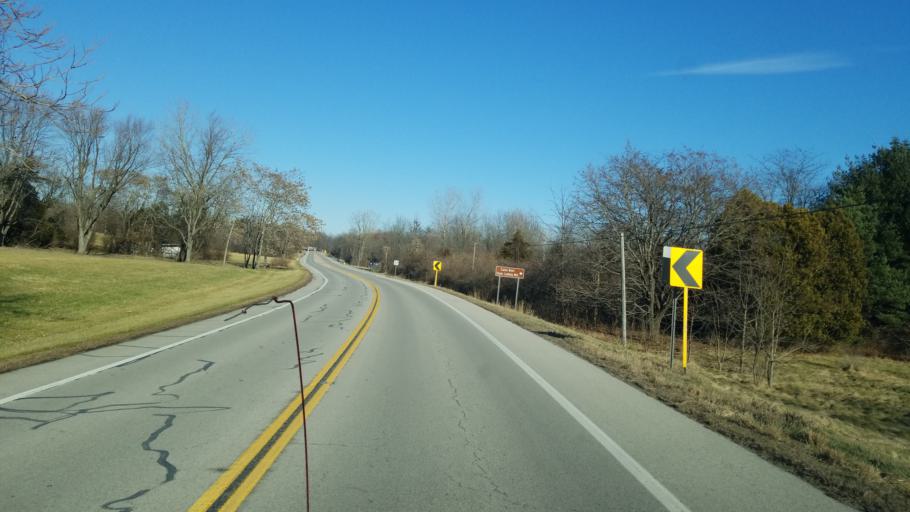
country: US
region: Ohio
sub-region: Wood County
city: Weston
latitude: 41.4175
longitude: -83.8571
